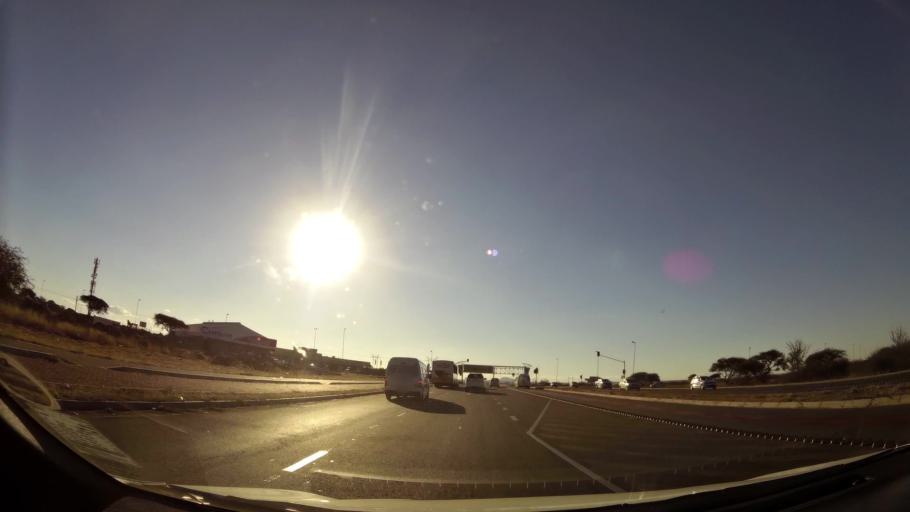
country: ZA
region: Limpopo
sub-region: Capricorn District Municipality
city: Polokwane
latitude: -23.8660
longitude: 29.4091
